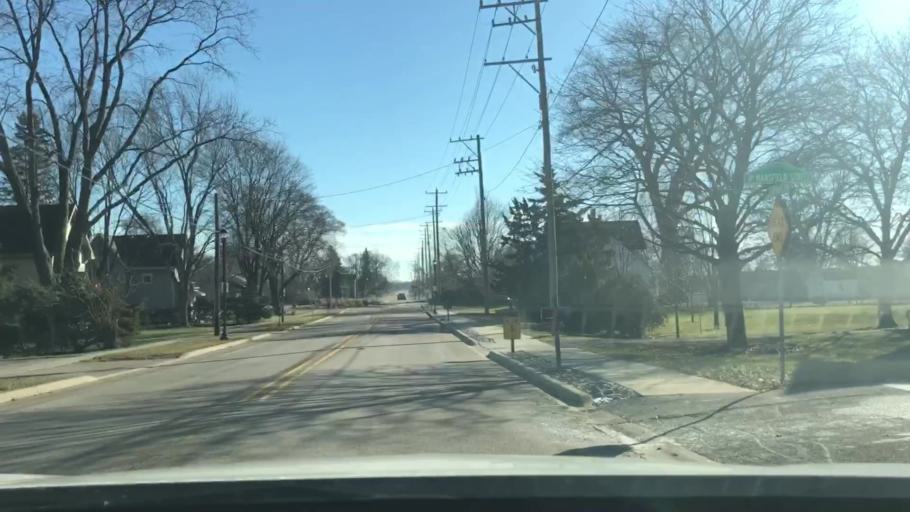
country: US
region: Illinois
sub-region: Kane County
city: Pingree Grove
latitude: 42.0698
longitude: -88.4146
